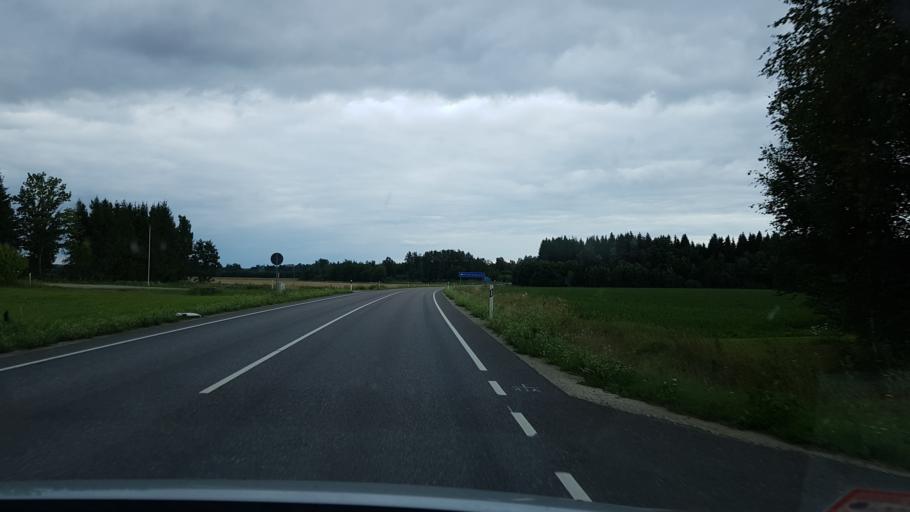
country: EE
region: Tartu
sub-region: Tartu linn
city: Tartu
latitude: 58.4095
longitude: 26.8941
